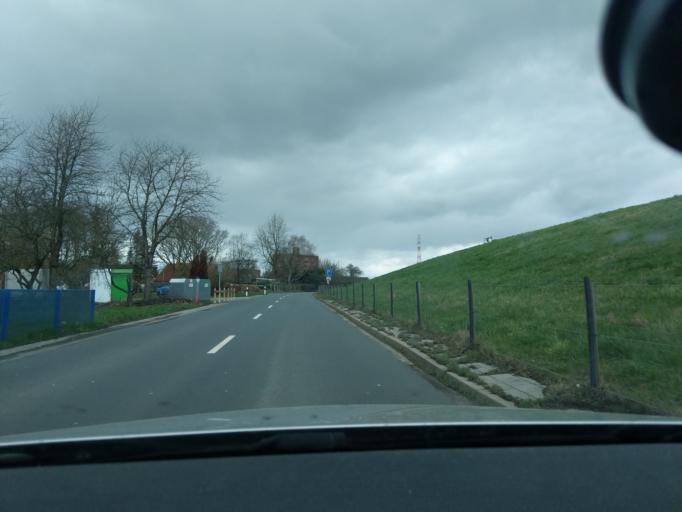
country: DE
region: Lower Saxony
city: Grunendeich
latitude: 53.5772
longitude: 9.6109
